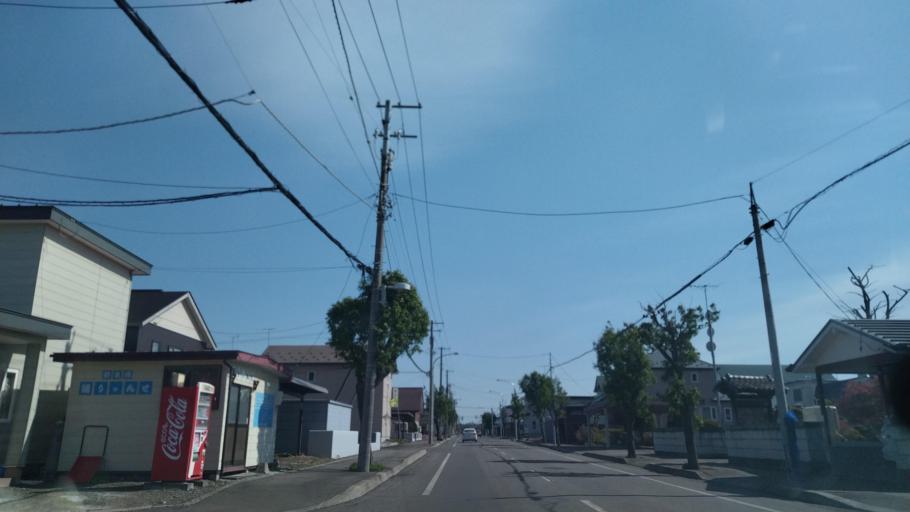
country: JP
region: Hokkaido
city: Obihiro
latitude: 42.9185
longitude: 143.0557
